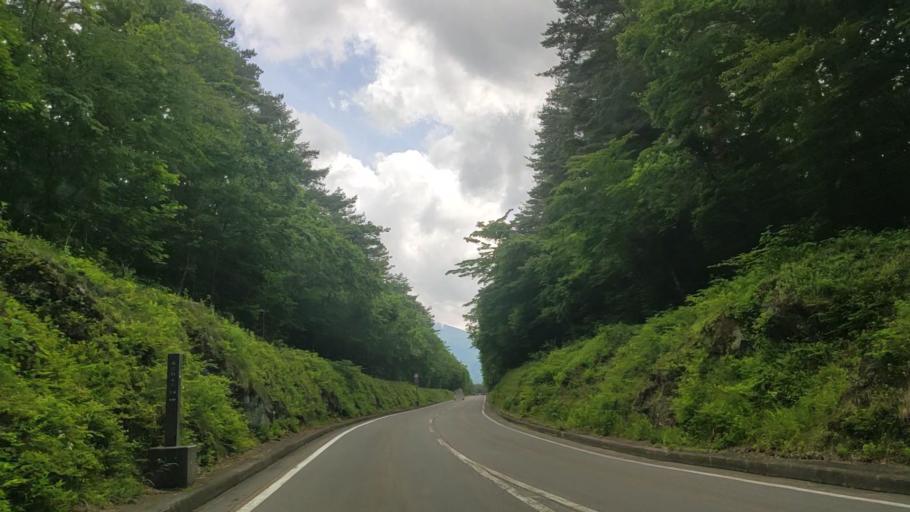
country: JP
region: Yamanashi
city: Fujikawaguchiko
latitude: 35.4516
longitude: 138.7584
